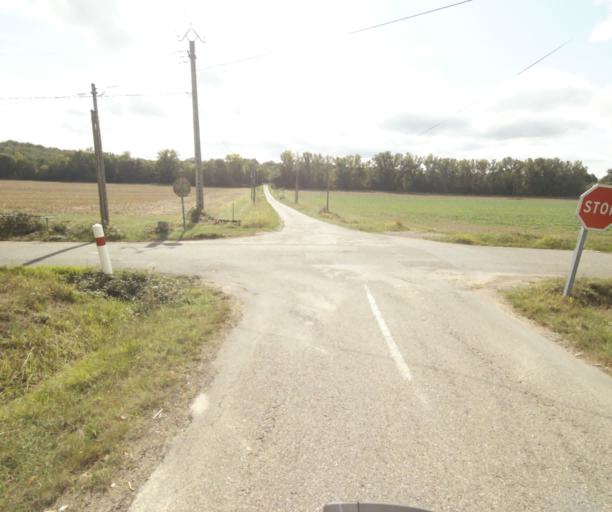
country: FR
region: Midi-Pyrenees
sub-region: Departement du Tarn-et-Garonne
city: Verdun-sur-Garonne
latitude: 43.8532
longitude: 1.1639
